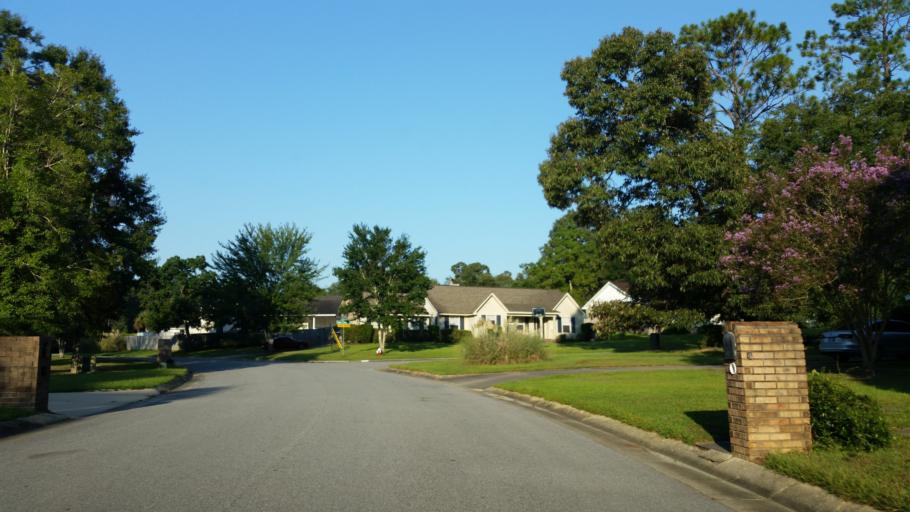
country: US
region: Florida
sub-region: Escambia County
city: Ensley
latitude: 30.5455
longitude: -87.2399
